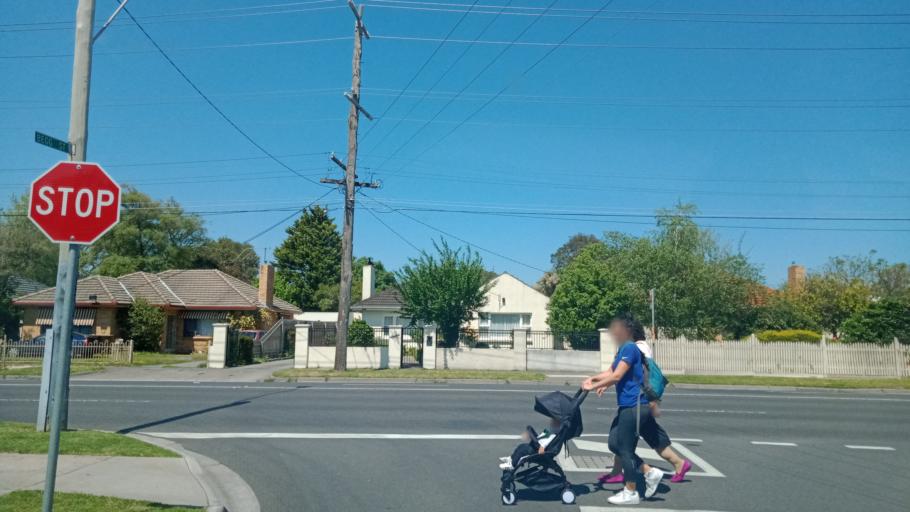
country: AU
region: Victoria
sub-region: Monash
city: Oakleigh South
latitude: -37.9232
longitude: 145.0765
